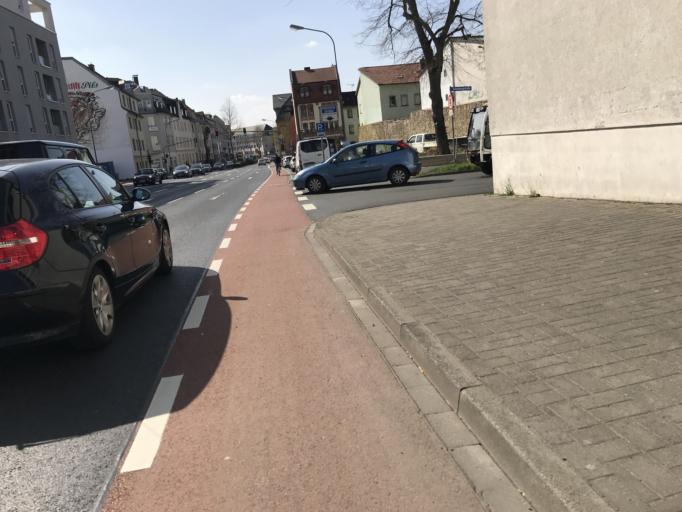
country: DE
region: Hesse
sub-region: Regierungsbezirk Kassel
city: Fulda
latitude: 50.5497
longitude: 9.6813
